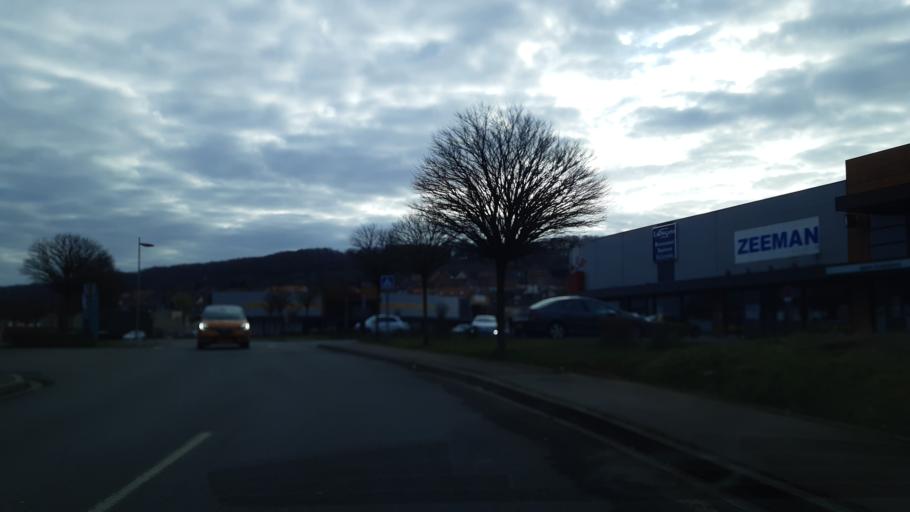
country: FR
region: Lorraine
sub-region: Departement de la Moselle
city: Audun-le-Tiche
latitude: 49.4754
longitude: 5.9541
